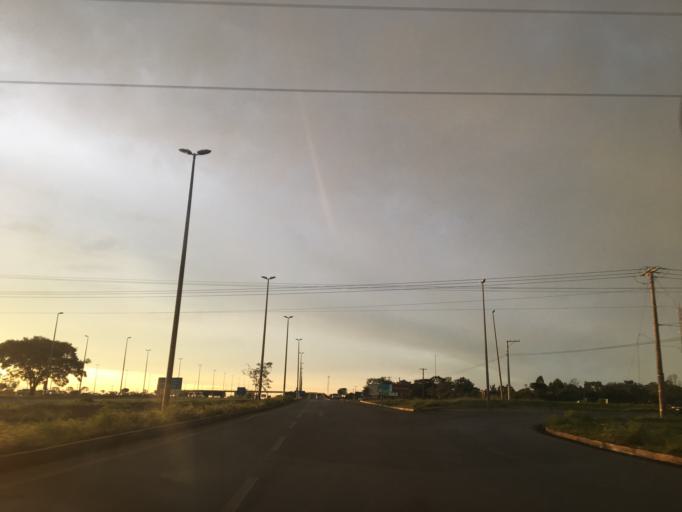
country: BR
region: Federal District
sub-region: Brasilia
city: Brasilia
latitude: -15.9759
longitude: -47.9906
